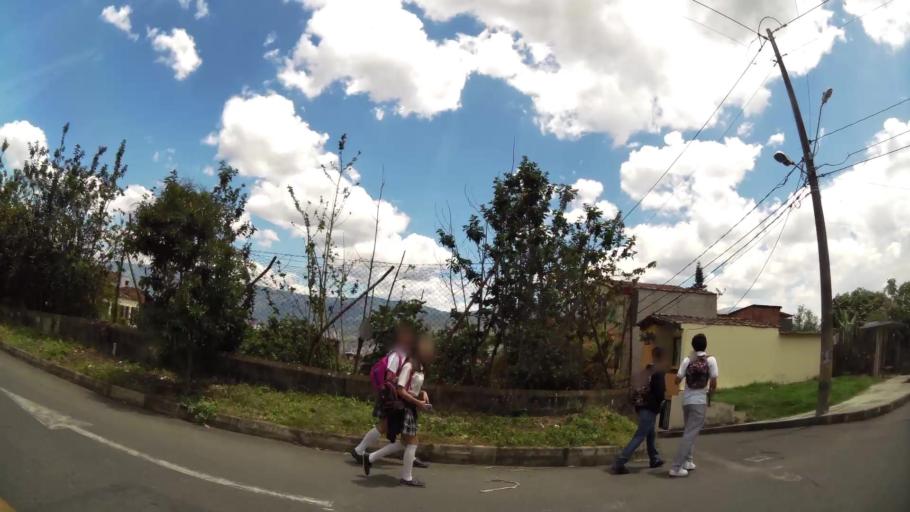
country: CO
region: Antioquia
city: La Estrella
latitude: 6.1564
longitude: -75.6460
